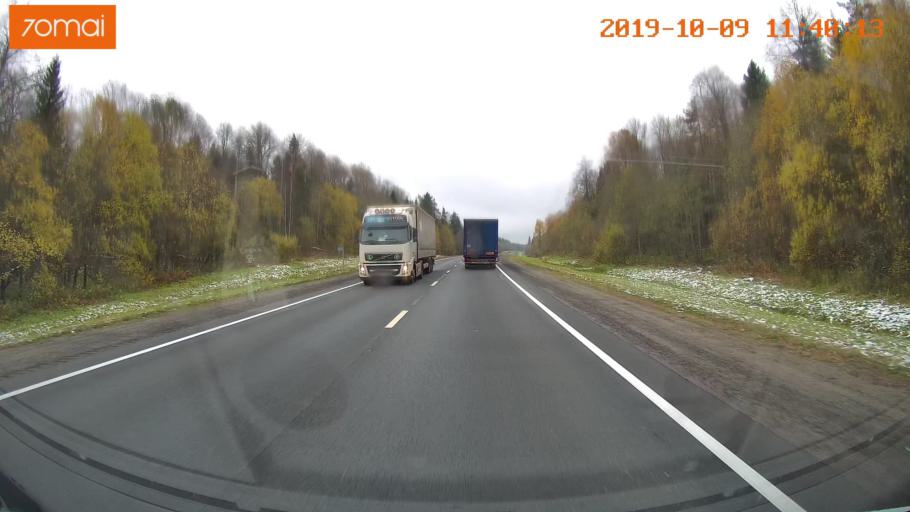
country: RU
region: Vologda
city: Gryazovets
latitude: 58.9456
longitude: 40.1731
